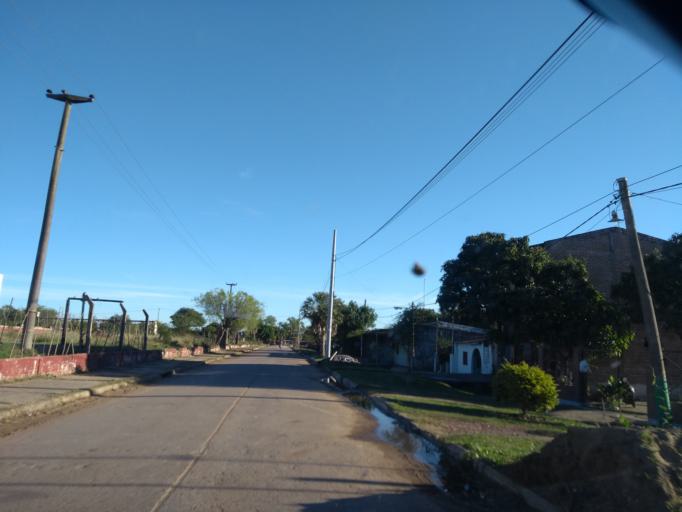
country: AR
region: Chaco
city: Puerto Vilelas
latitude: -27.4996
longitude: -58.9331
